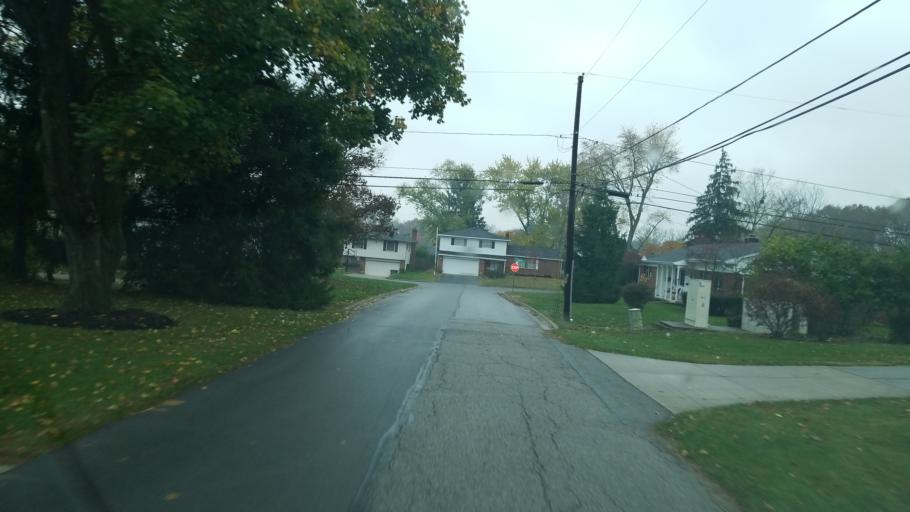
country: US
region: Ohio
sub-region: Franklin County
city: Upper Arlington
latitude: 40.0385
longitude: -83.0448
